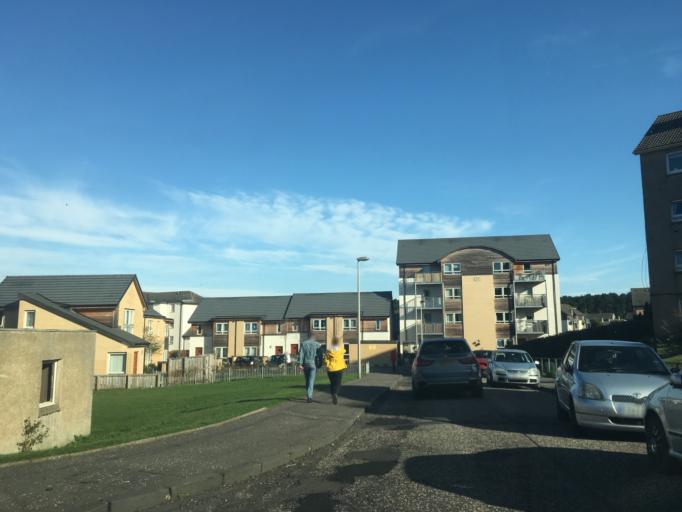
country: GB
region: Scotland
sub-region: Edinburgh
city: Colinton
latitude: 55.9103
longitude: -3.2234
